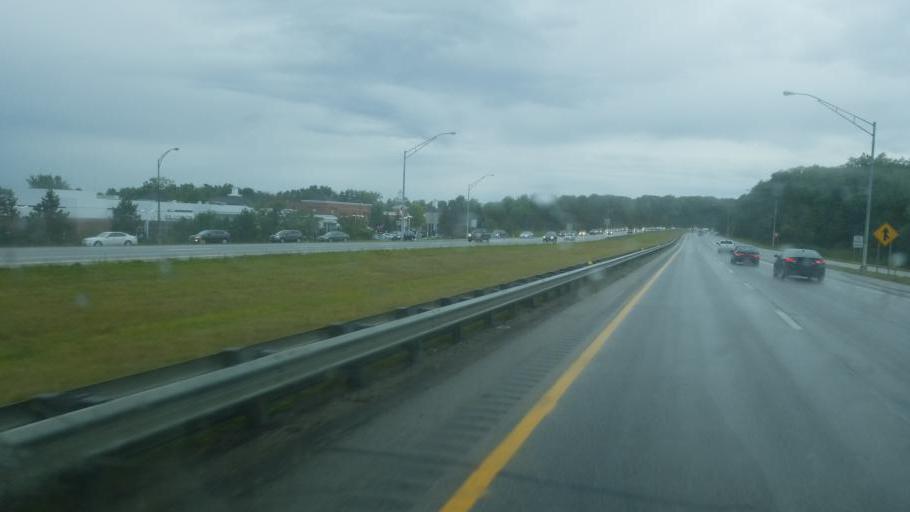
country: US
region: Ohio
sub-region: Cuyahoga County
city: Solon
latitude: 41.3949
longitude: -81.4397
